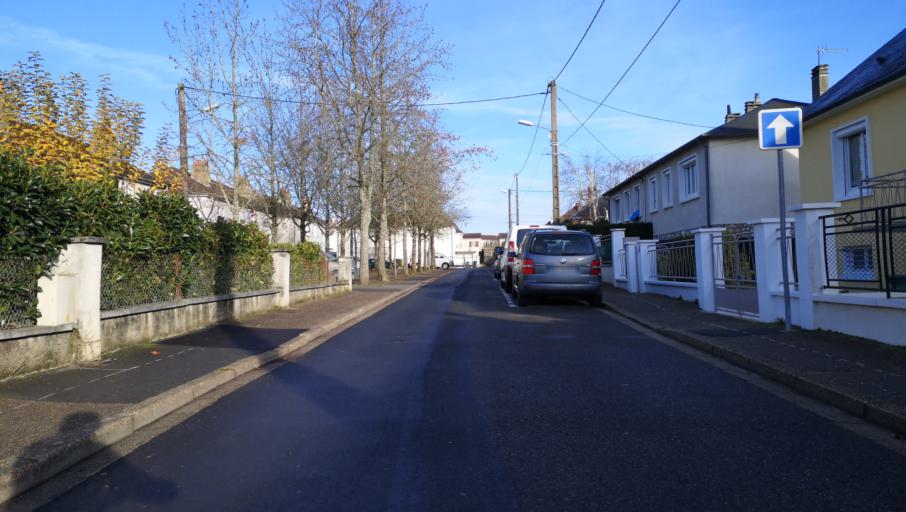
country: FR
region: Centre
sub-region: Departement du Loiret
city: Semoy
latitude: 47.9190
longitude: 1.9389
